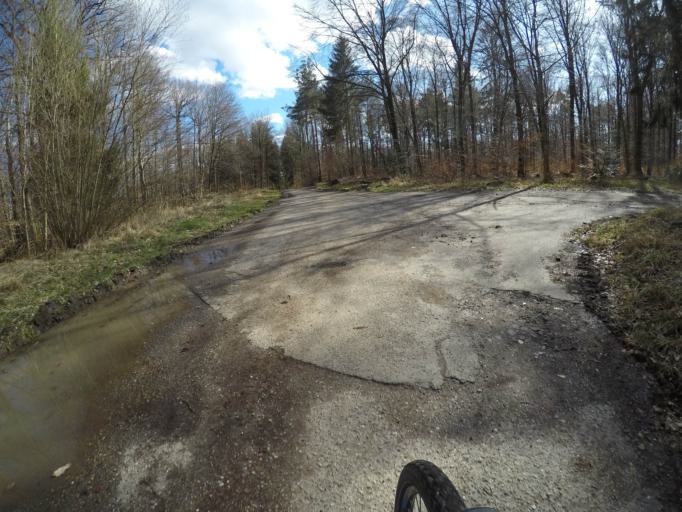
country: DE
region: Baden-Wuerttemberg
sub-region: Regierungsbezirk Stuttgart
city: Leinfelden-Echterdingen
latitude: 48.6812
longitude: 9.1462
